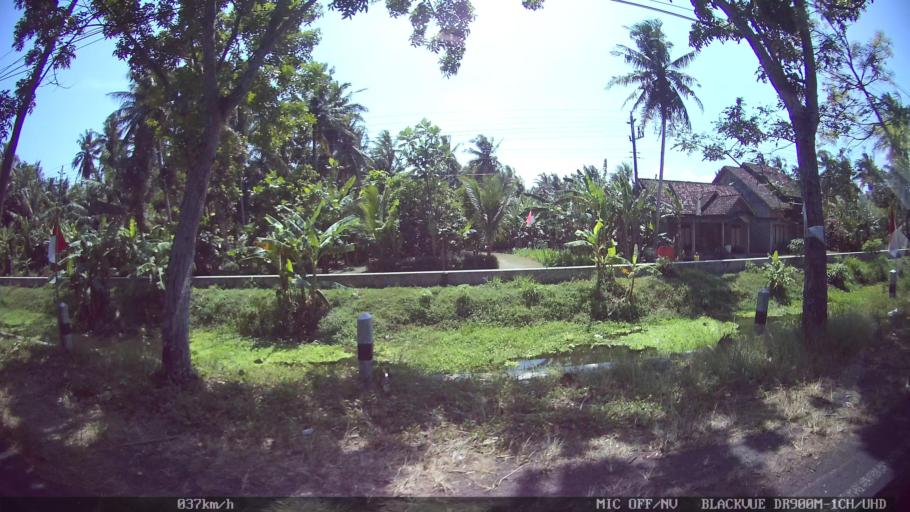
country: ID
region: Daerah Istimewa Yogyakarta
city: Srandakan
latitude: -7.9369
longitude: 110.1534
